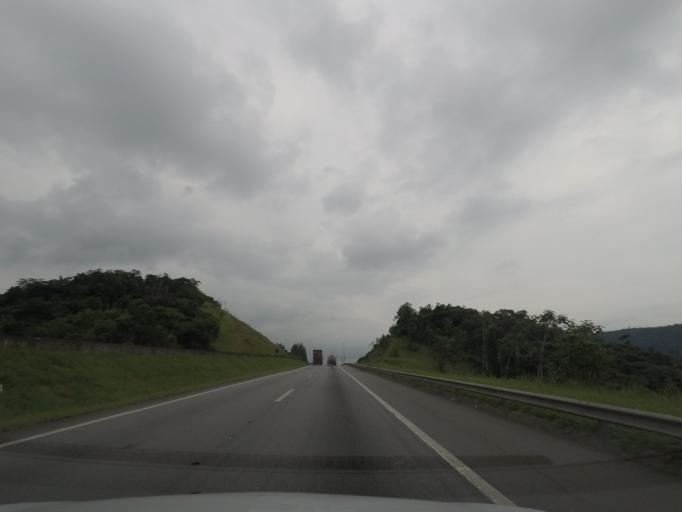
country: BR
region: Sao Paulo
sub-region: Miracatu
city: Miracatu
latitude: -24.1676
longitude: -47.3358
